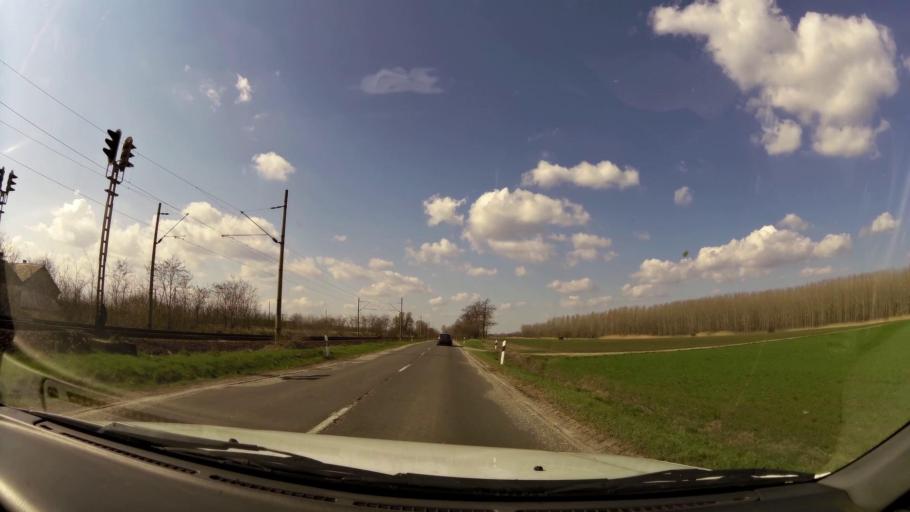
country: HU
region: Pest
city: Farmos
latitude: 47.3776
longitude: 19.7912
